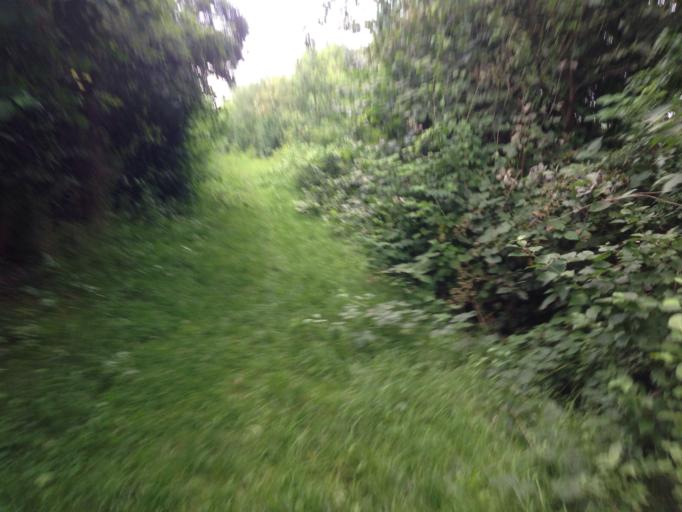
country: DE
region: North Rhine-Westphalia
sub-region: Regierungsbezirk Munster
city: Muenster
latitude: 52.0005
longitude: 7.5700
